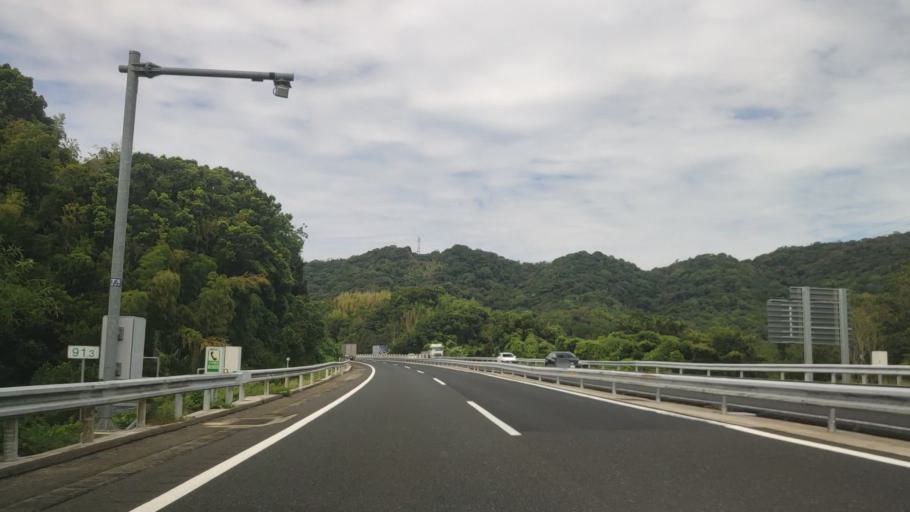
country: JP
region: Wakayama
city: Wakayama-shi
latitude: 34.2172
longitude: 135.2234
